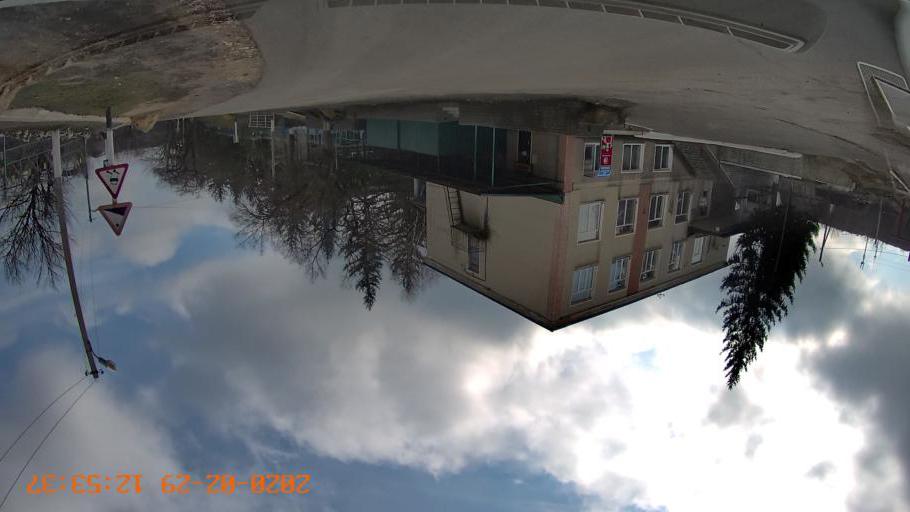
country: MD
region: Telenesti
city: Camenca
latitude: 48.1051
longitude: 28.7331
